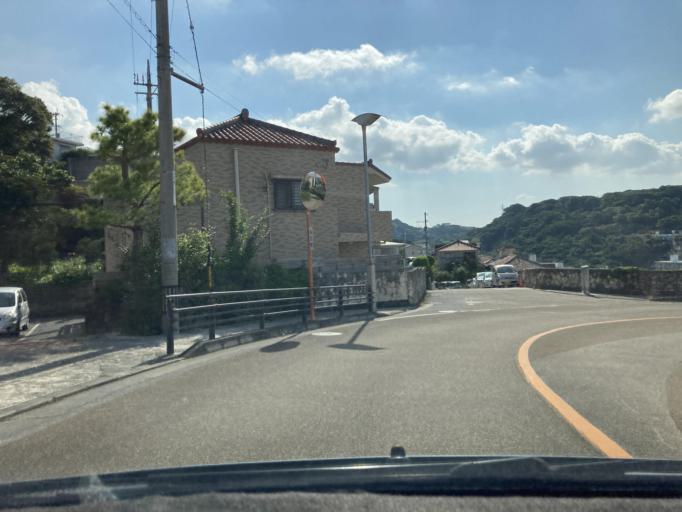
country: JP
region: Okinawa
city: Naha-shi
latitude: 26.2168
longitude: 127.7129
